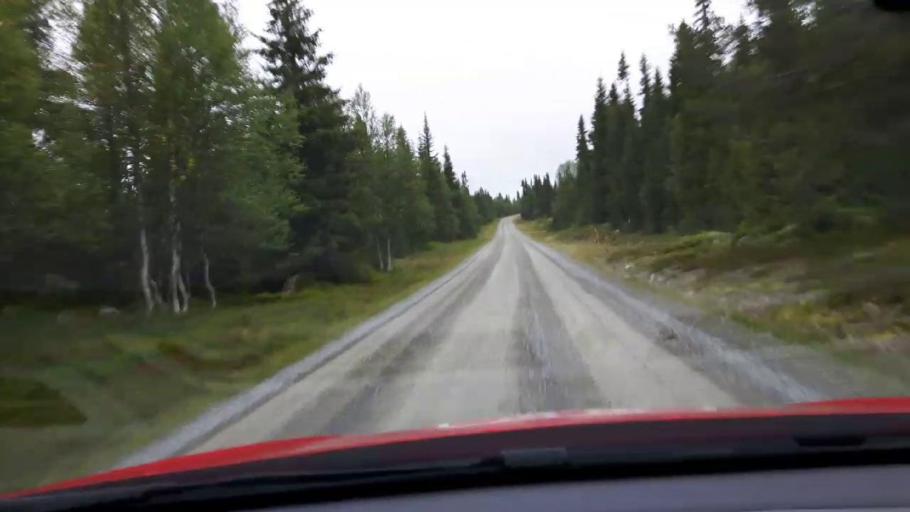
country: SE
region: Jaemtland
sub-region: Bergs Kommun
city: Hoverberg
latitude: 62.8622
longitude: 13.9468
